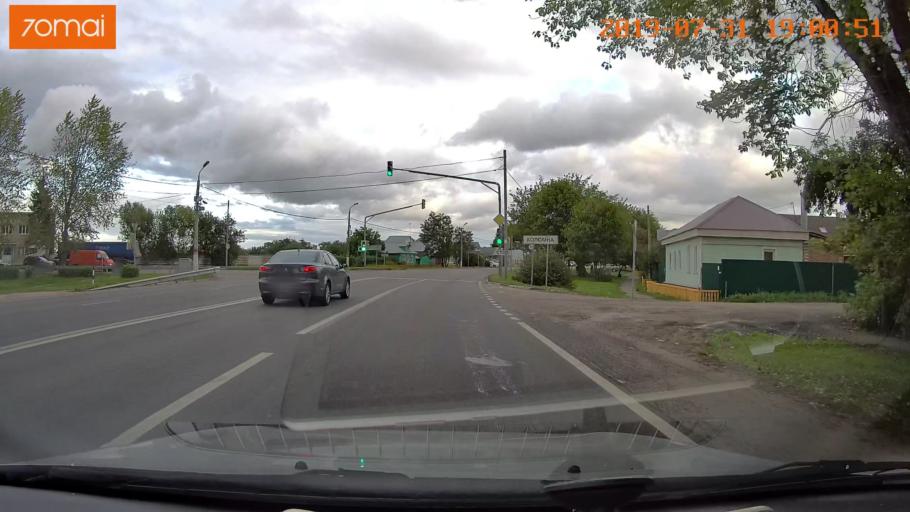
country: RU
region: Moskovskaya
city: Raduzhnyy
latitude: 55.1308
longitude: 38.7275
